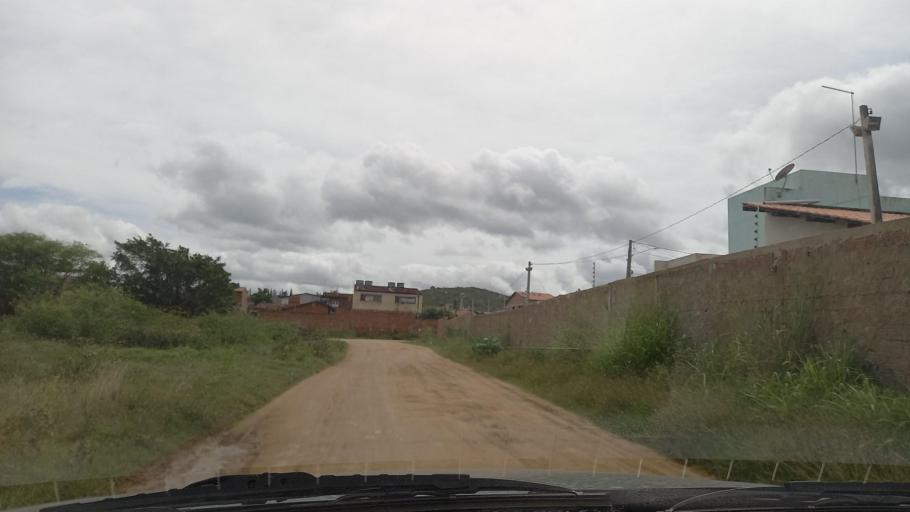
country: ET
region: Oromiya
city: Gore
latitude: 8.1909
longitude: 35.5796
